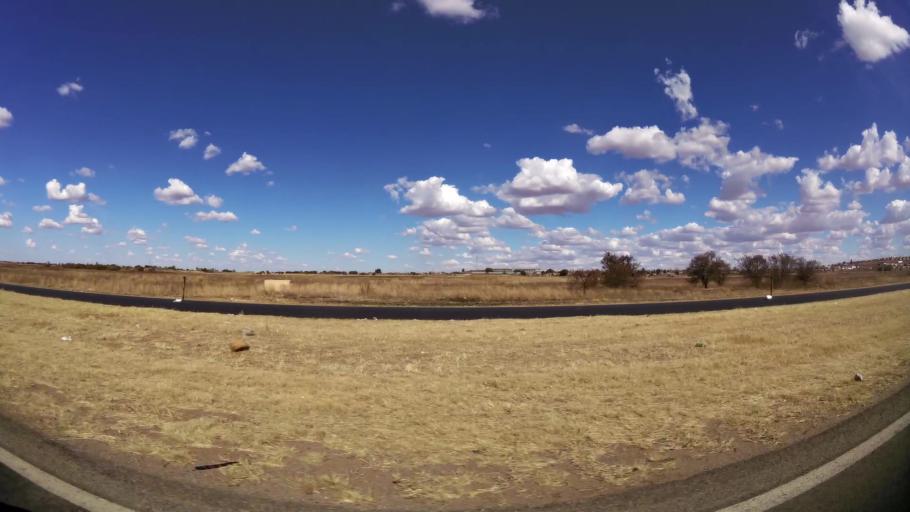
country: ZA
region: North-West
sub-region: Dr Kenneth Kaunda District Municipality
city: Klerksdorp
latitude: -26.8727
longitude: 26.6070
